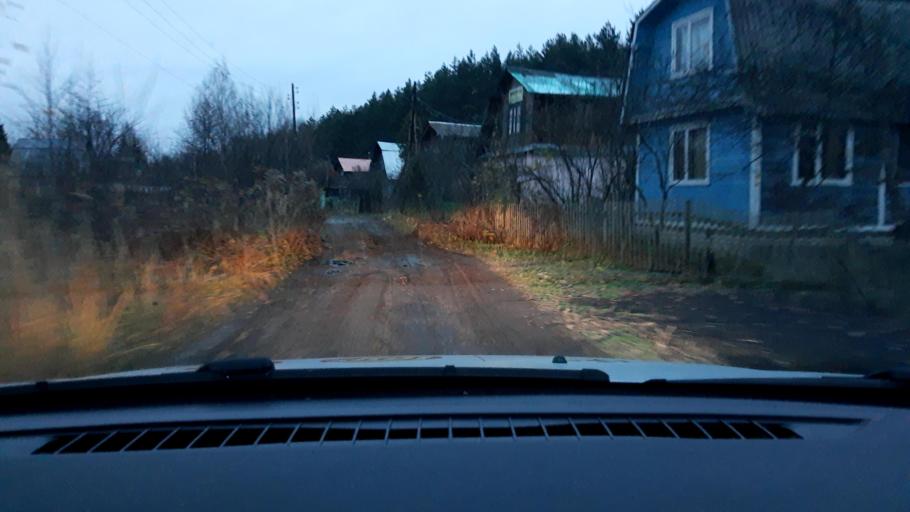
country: RU
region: Nizjnij Novgorod
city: Neklyudovo
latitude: 56.4273
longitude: 44.0091
